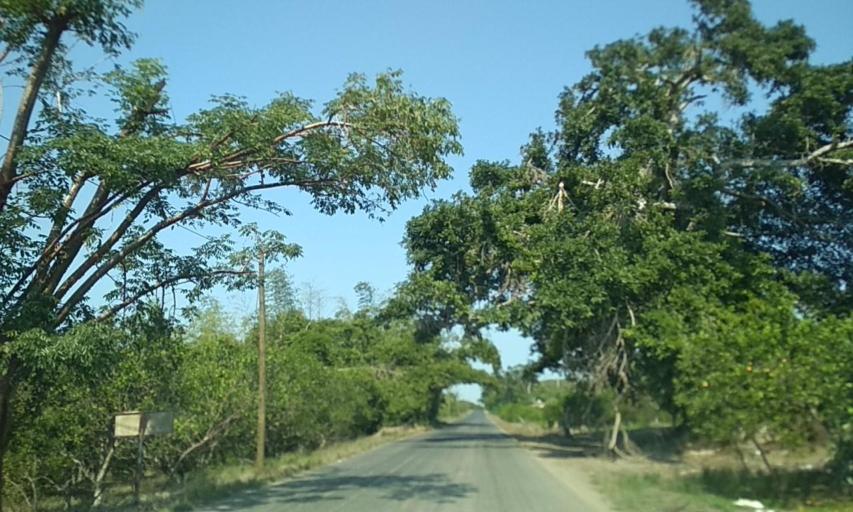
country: MX
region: Veracruz
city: Gutierrez Zamora
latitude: 20.3530
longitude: -97.1539
